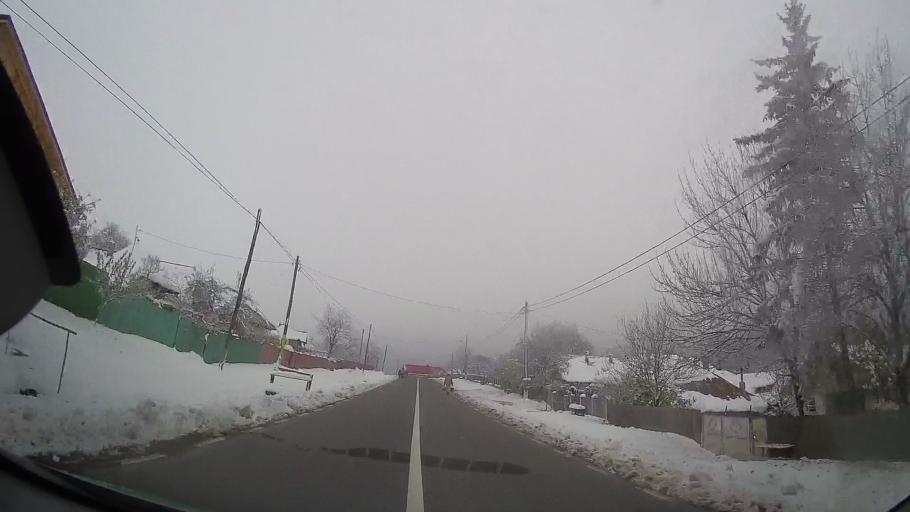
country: RO
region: Neamt
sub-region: Comuna Poenari
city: Poienari
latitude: 46.8802
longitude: 27.1321
